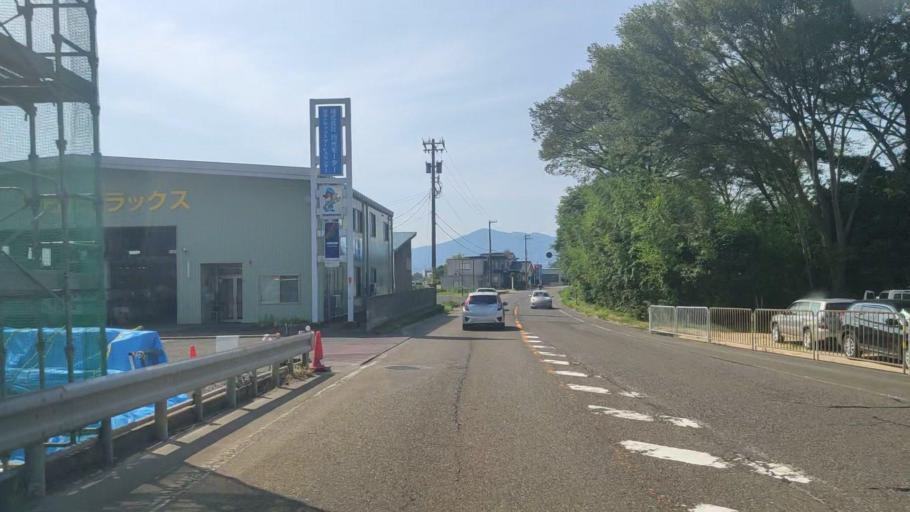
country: JP
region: Fukui
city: Tsuruga
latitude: 35.6243
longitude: 136.0763
